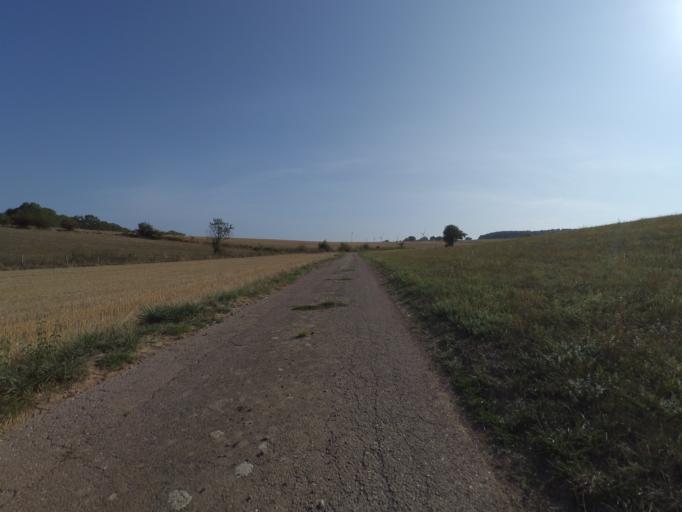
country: DE
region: Rheinland-Pfalz
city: Kirf
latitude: 49.5502
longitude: 6.4390
